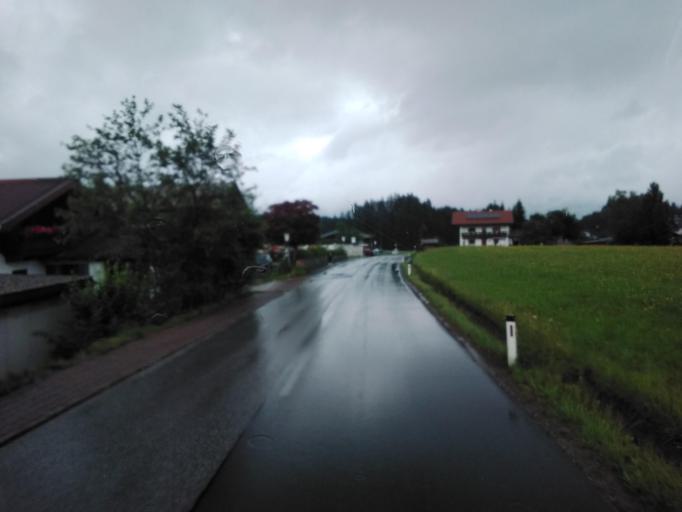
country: AT
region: Tyrol
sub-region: Politischer Bezirk Kitzbuhel
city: Schwendt
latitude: 47.6392
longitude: 12.3928
